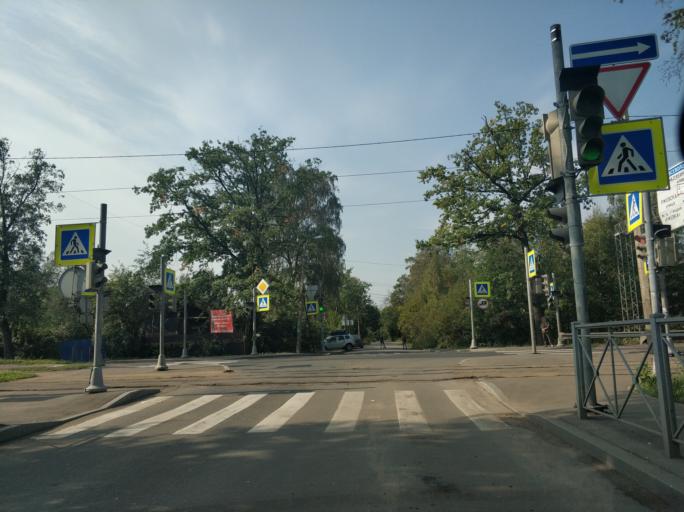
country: RU
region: St.-Petersburg
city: Krasnogvargeisky
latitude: 59.9769
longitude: 30.5063
